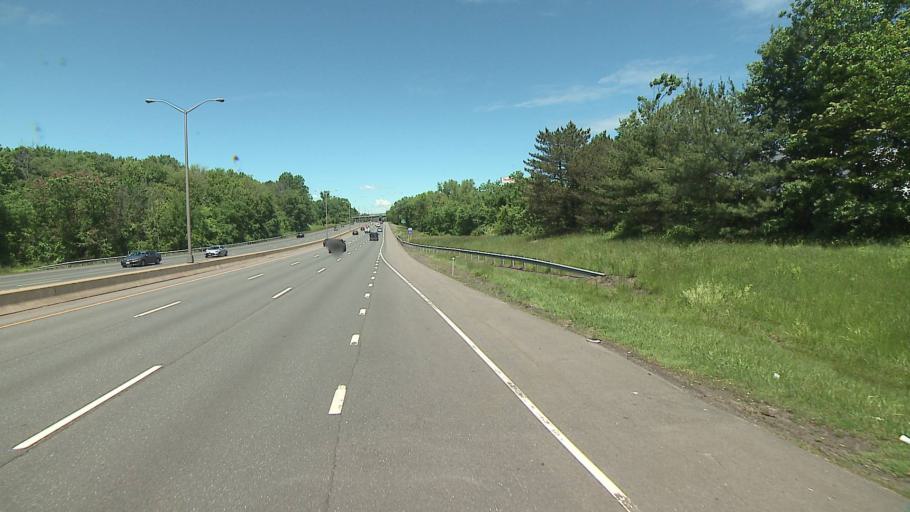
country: US
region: Connecticut
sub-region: Hartford County
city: Windsor Locks
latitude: 41.9337
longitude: -72.6079
